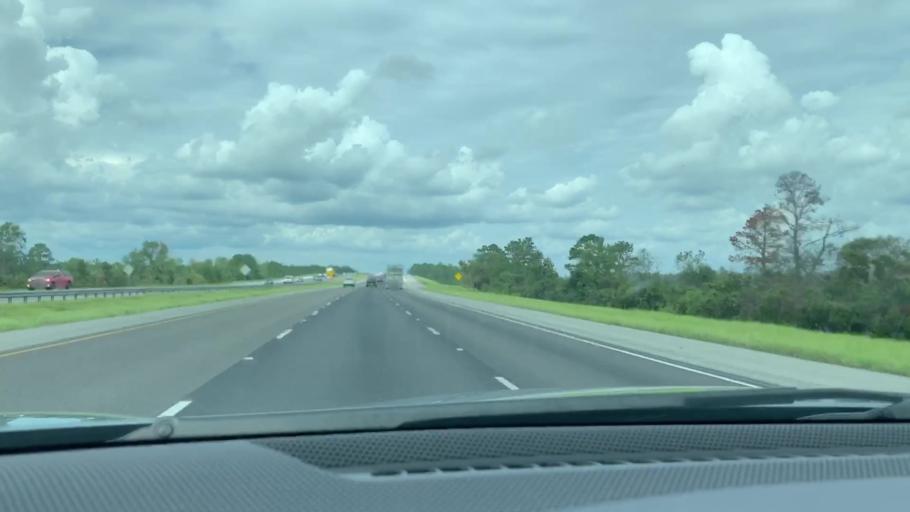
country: US
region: Georgia
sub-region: Liberty County
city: Midway
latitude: 31.7311
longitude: -81.3878
